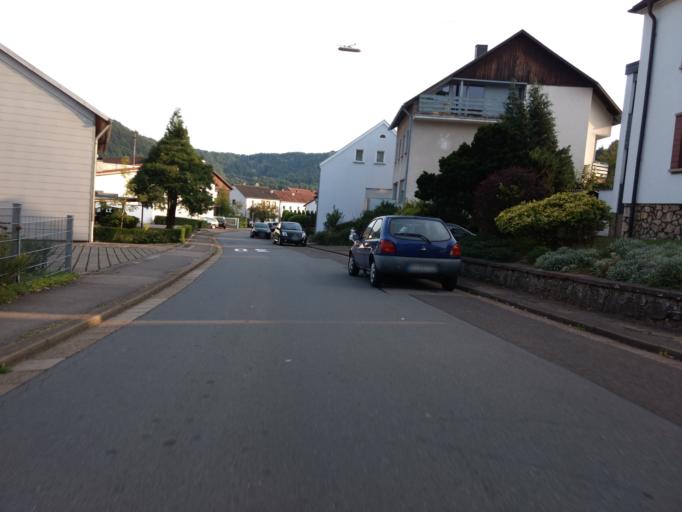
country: DE
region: Saarland
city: Rehlingen-Siersburg
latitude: 49.3566
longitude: 6.6680
